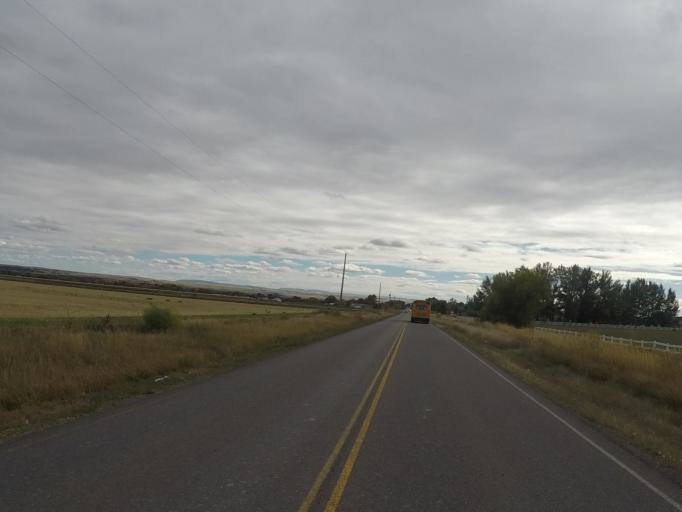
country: US
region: Montana
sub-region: Yellowstone County
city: Laurel
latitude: 45.7501
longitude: -108.6589
